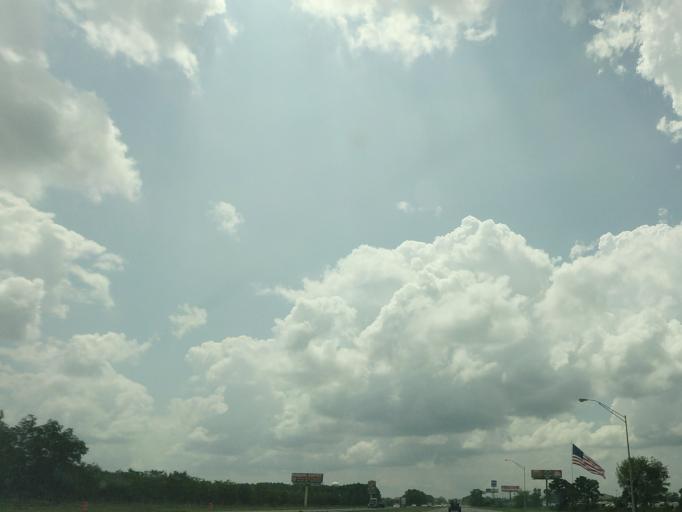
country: US
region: Georgia
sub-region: Peach County
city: Byron
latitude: 32.6563
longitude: -83.7443
